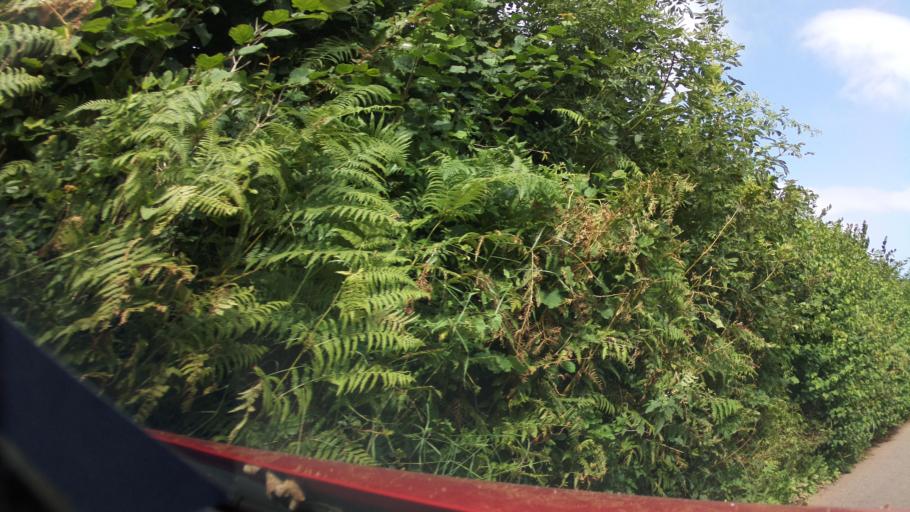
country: GB
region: England
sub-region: Devon
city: Marldon
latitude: 50.4146
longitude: -3.6236
